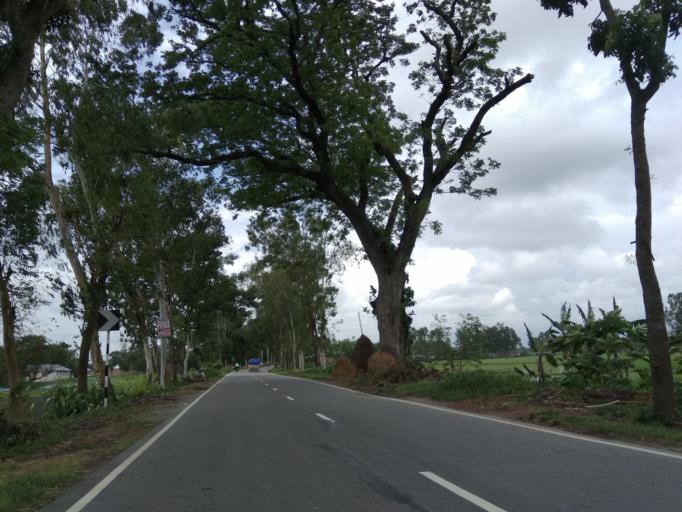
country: BD
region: Rajshahi
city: Saidpur
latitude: 25.7699
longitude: 88.8056
